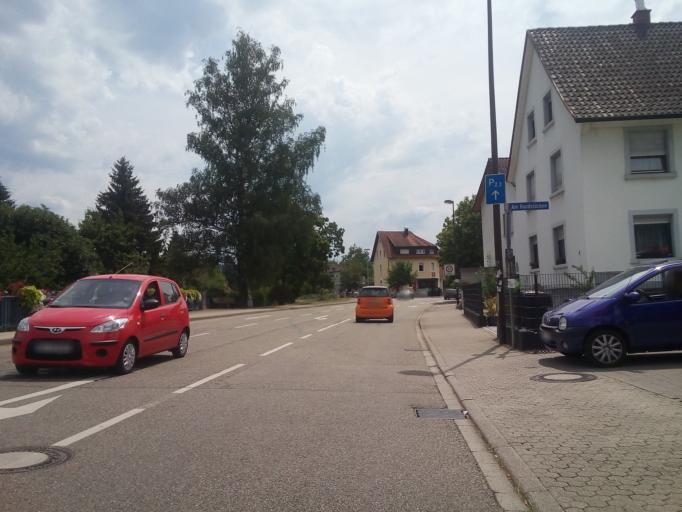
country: DE
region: Baden-Wuerttemberg
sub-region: Freiburg Region
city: Achern
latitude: 48.6279
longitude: 8.0680
